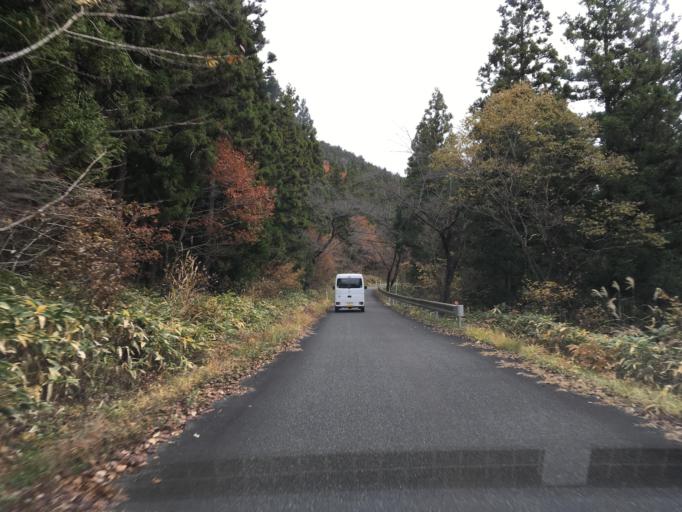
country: JP
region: Iwate
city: Mizusawa
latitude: 39.1245
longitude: 141.3152
